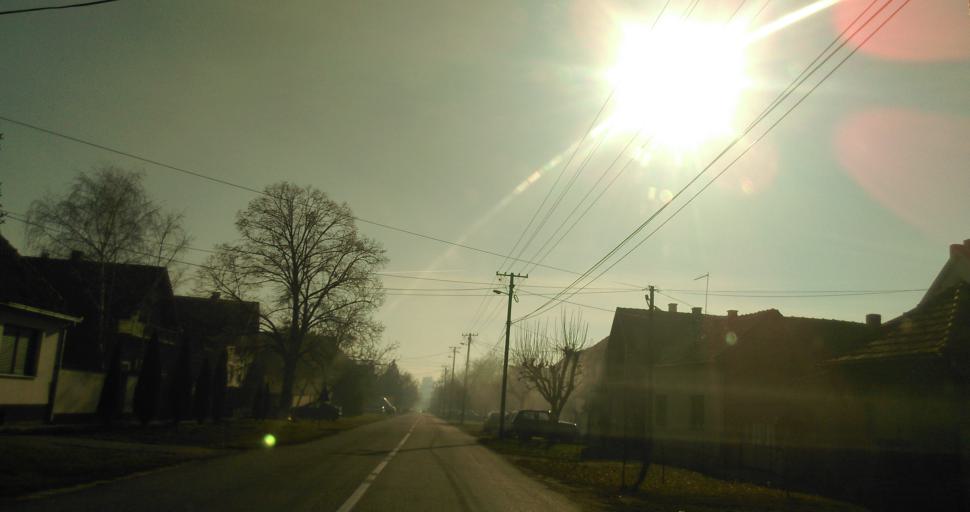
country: RS
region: Autonomna Pokrajina Vojvodina
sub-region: Sremski Okrug
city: Ruma
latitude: 45.0154
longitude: 19.8297
